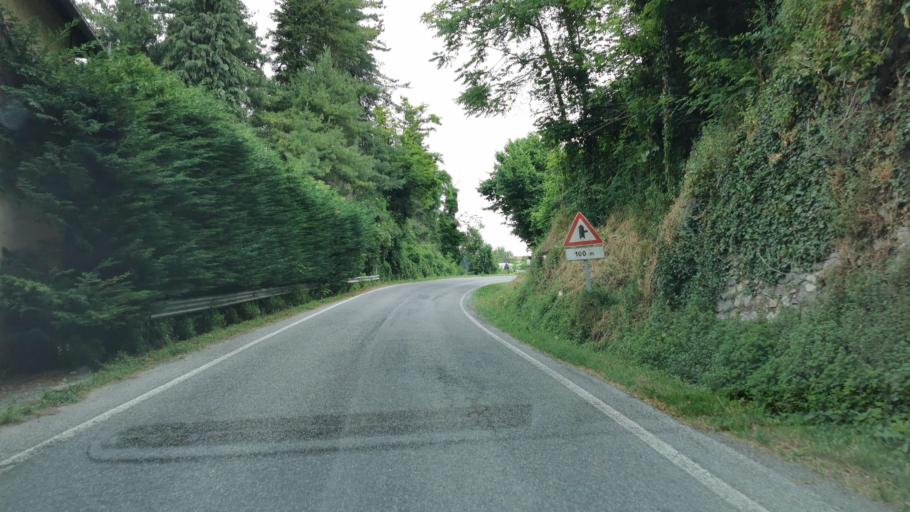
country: IT
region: Piedmont
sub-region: Provincia di Cuneo
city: Sale San Giovanni
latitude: 44.4003
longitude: 8.0775
